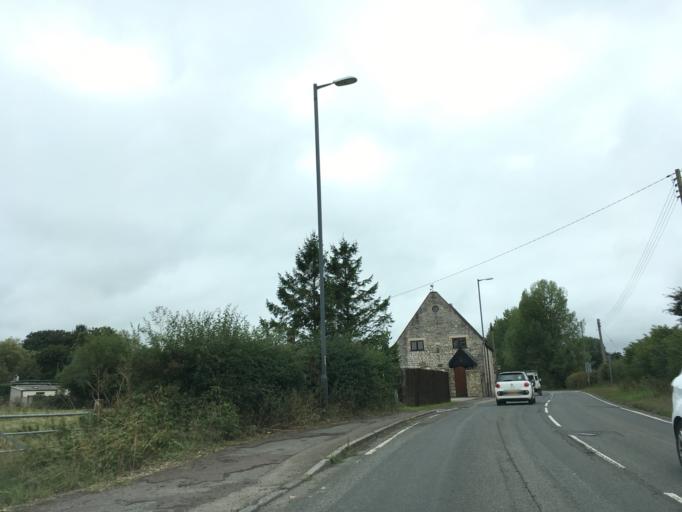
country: GB
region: England
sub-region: Bath and North East Somerset
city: Timsbury
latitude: 51.3420
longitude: -2.4952
